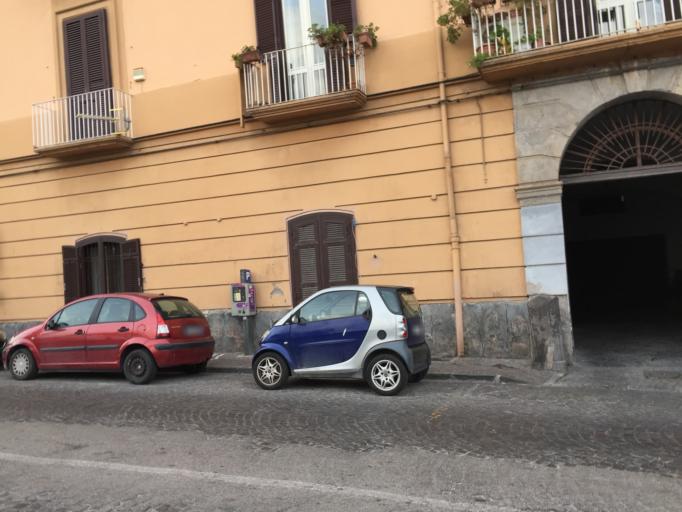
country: IT
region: Campania
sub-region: Provincia di Napoli
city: Bagnoli
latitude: 40.8156
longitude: 14.2097
